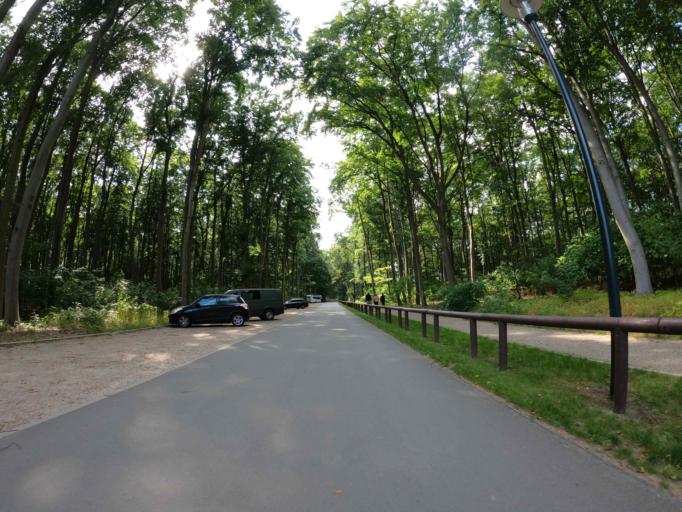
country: DE
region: Mecklenburg-Vorpommern
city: Malchow
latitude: 53.4854
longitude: 12.4346
